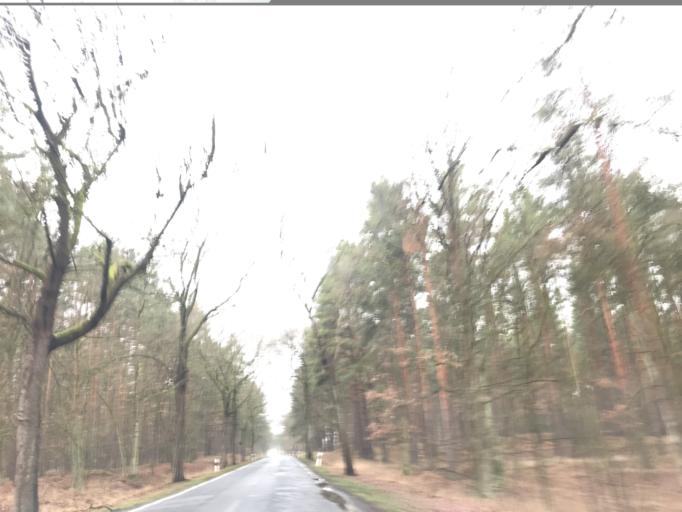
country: DE
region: Brandenburg
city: Brieselang
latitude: 52.6799
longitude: 12.9548
